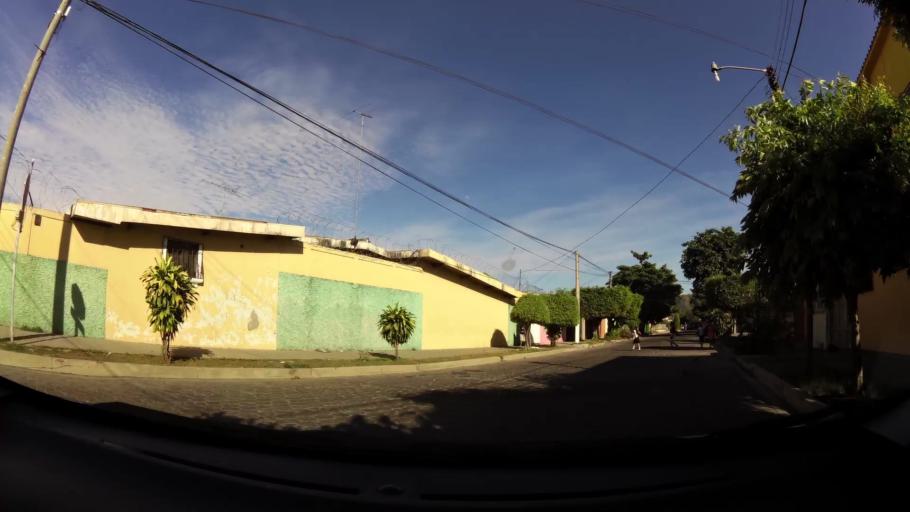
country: SV
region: Santa Ana
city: Santa Ana
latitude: 13.9999
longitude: -89.5610
